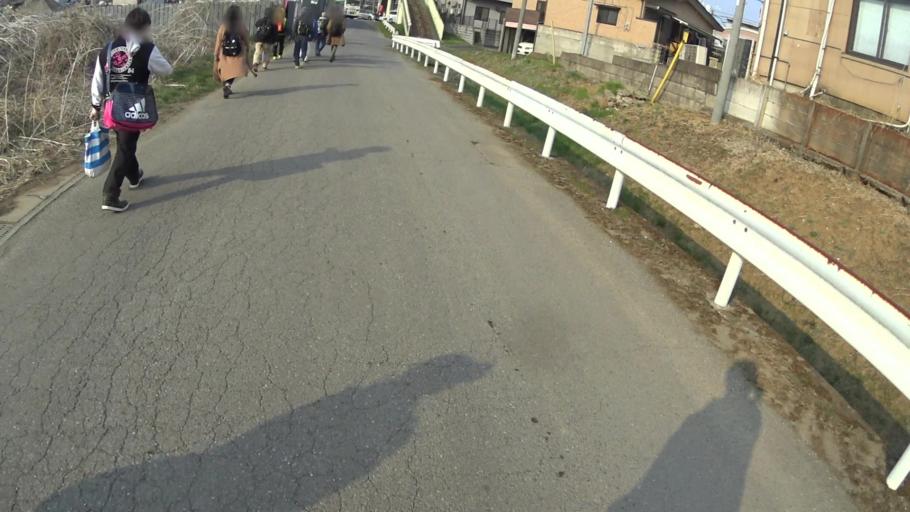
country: JP
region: Ibaraki
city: Koga
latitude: 36.1839
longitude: 139.7006
